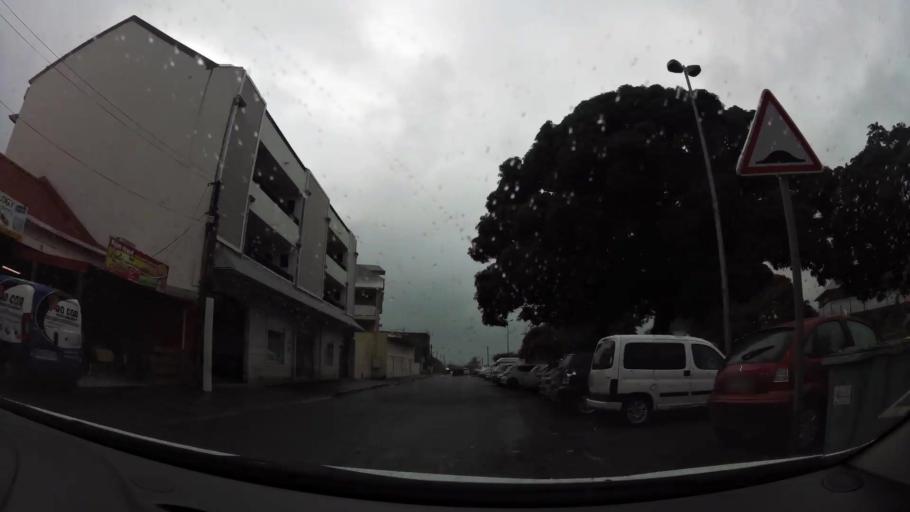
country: RE
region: Reunion
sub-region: Reunion
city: Saint-Andre
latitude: -20.9589
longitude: 55.6540
